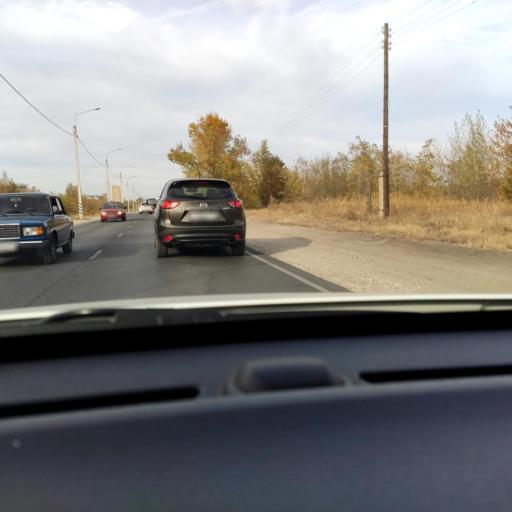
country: RU
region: Voronezj
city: Maslovka
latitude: 51.5783
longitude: 39.2471
